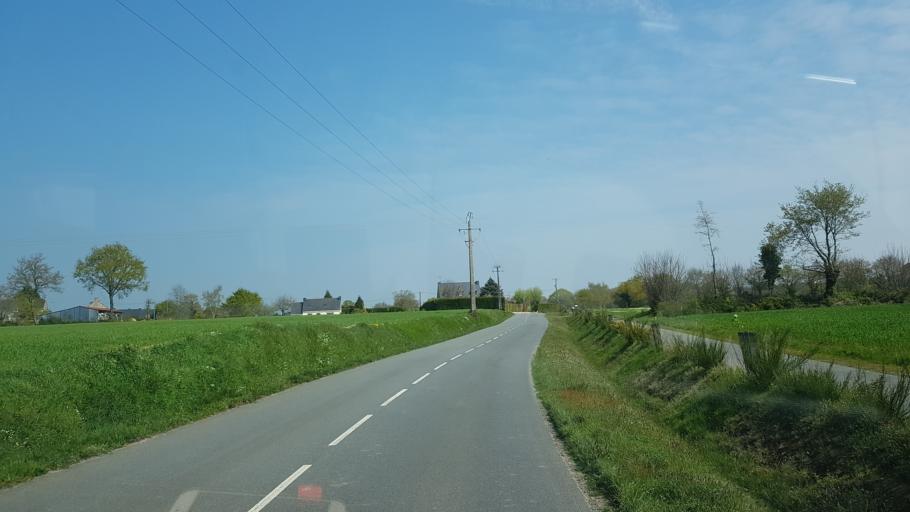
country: FR
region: Brittany
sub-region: Departement du Morbihan
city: Noyal-Muzillac
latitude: 47.5870
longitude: -2.4059
